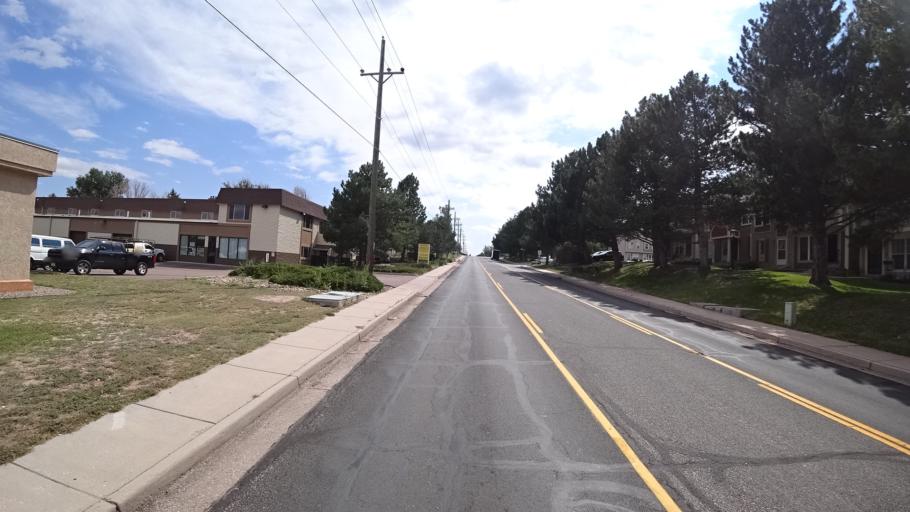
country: US
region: Colorado
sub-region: El Paso County
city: Cimarron Hills
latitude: 38.8852
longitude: -104.7608
